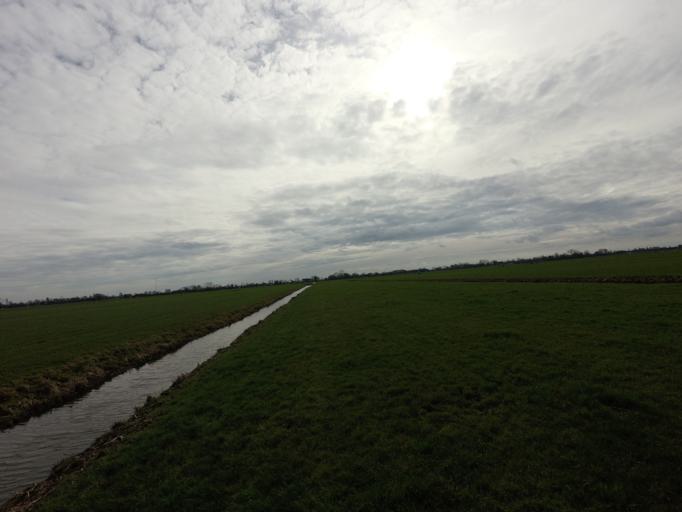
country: NL
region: Utrecht
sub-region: Gemeente Oudewater
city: Oudewater
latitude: 51.9945
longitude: 4.8768
